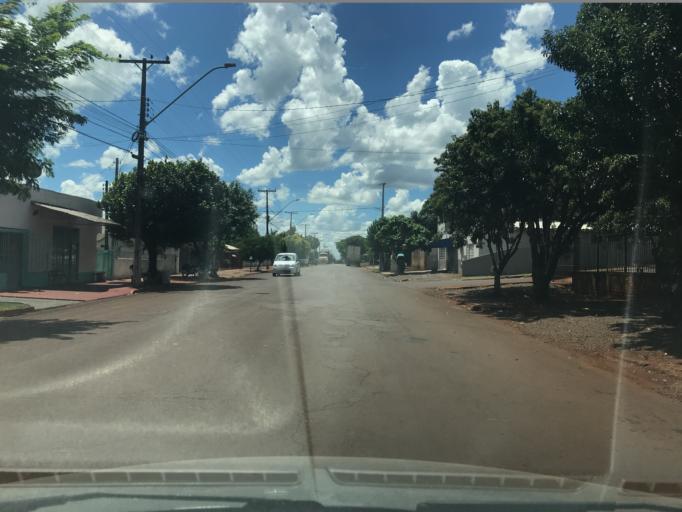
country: BR
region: Parana
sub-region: Palotina
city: Palotina
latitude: -24.2744
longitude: -53.8485
